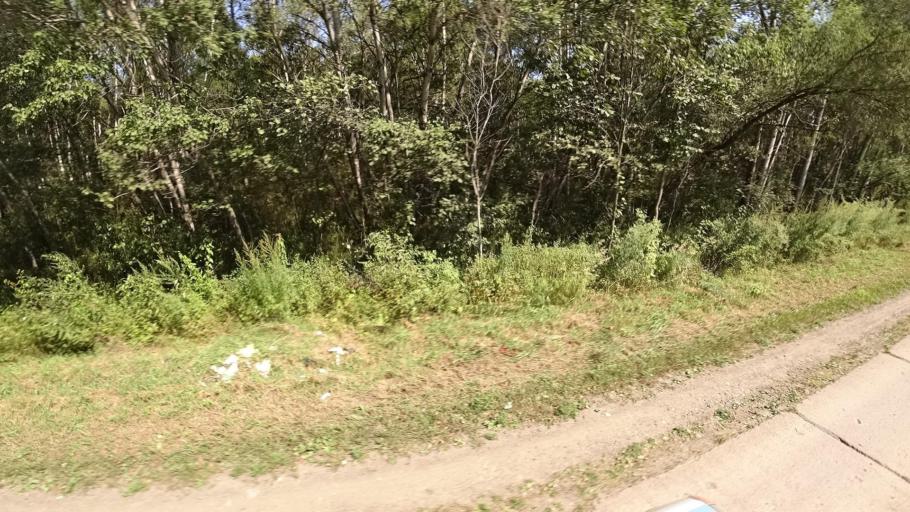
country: RU
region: Khabarovsk Krai
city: Khor
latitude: 47.9890
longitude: 135.0950
